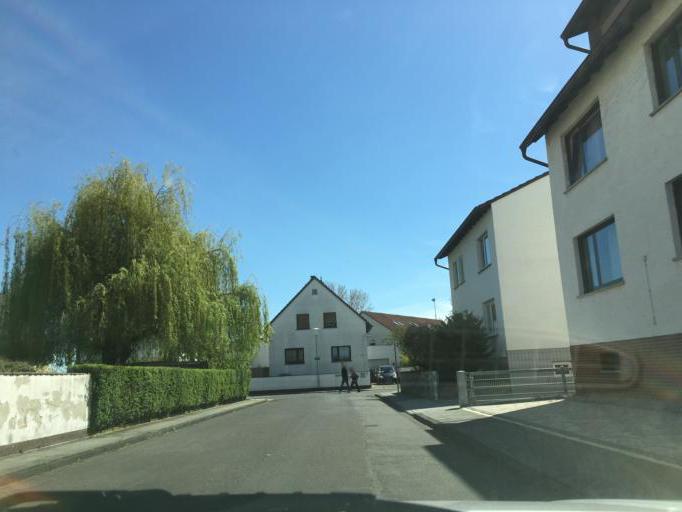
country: DE
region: Hesse
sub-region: Regierungsbezirk Darmstadt
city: Gross-Zimmern
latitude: 49.8783
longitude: 8.8190
